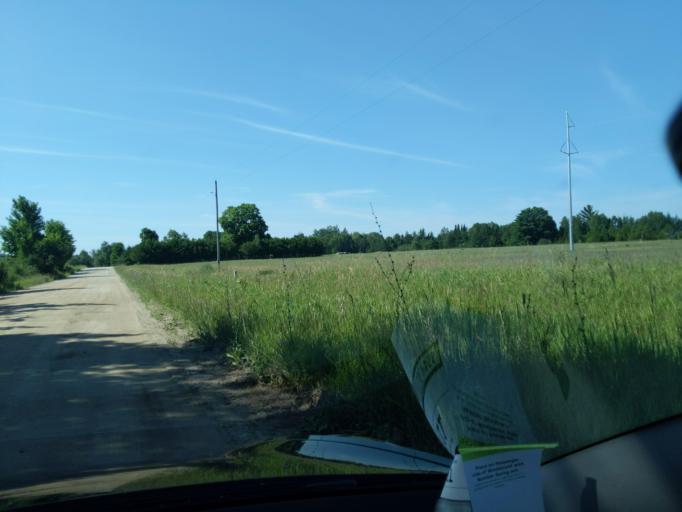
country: US
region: Michigan
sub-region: Cheboygan County
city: Cheboygan
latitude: 45.6534
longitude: -84.6303
